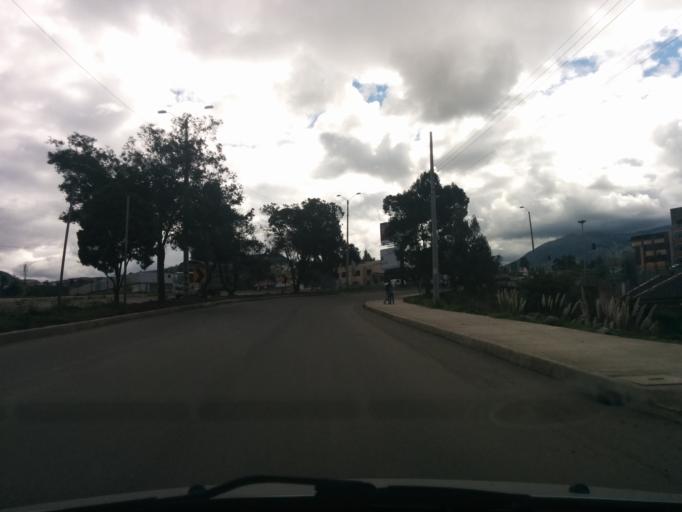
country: EC
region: Azuay
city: Cuenca
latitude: -2.9250
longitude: -79.0391
